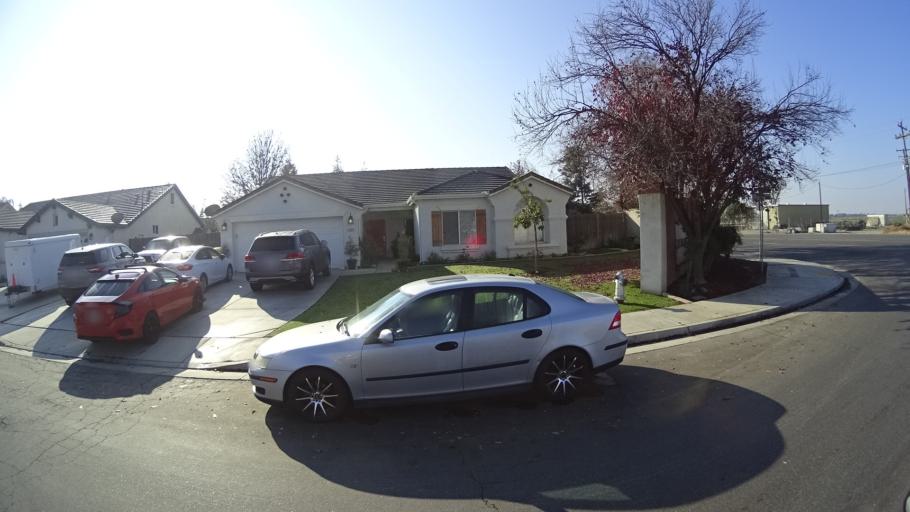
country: US
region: California
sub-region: Kern County
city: Greenacres
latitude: 35.3091
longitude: -119.1277
